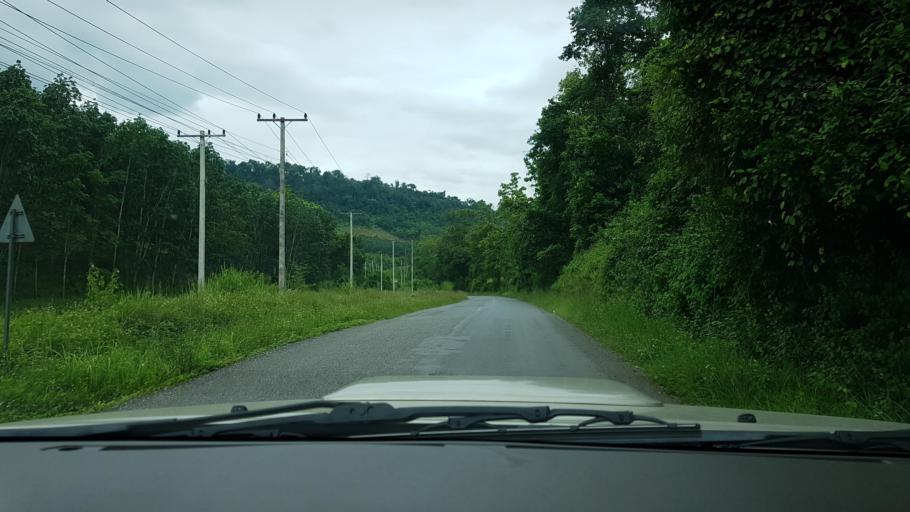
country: LA
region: Loungnamtha
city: Muang Nale
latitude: 20.1847
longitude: 101.5195
